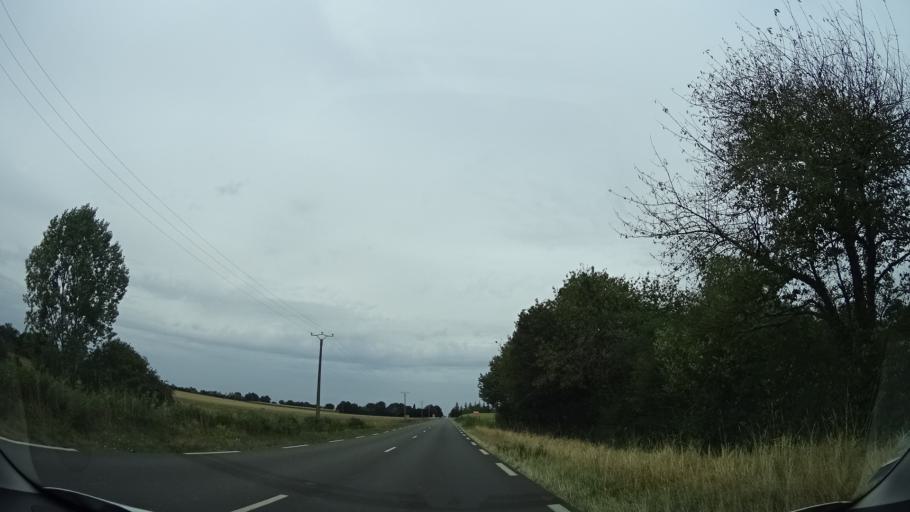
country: FR
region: Pays de la Loire
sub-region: Departement de la Mayenne
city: Meslay-du-Maine
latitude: 47.9605
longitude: -0.5723
